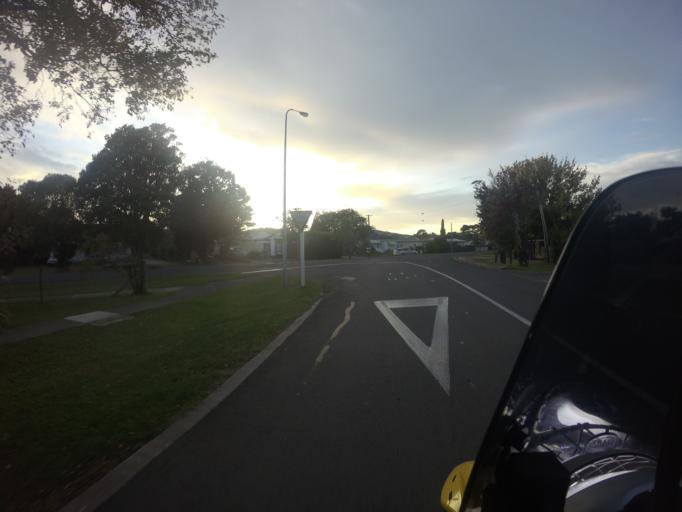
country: NZ
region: Gisborne
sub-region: Gisborne District
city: Gisborne
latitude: -38.6698
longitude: 178.0428
